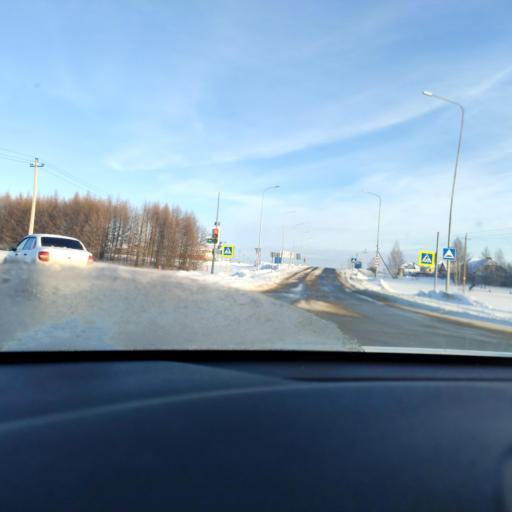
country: RU
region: Tatarstan
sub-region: Arskiy Rayon
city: Arsk
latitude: 56.1064
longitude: 49.8954
